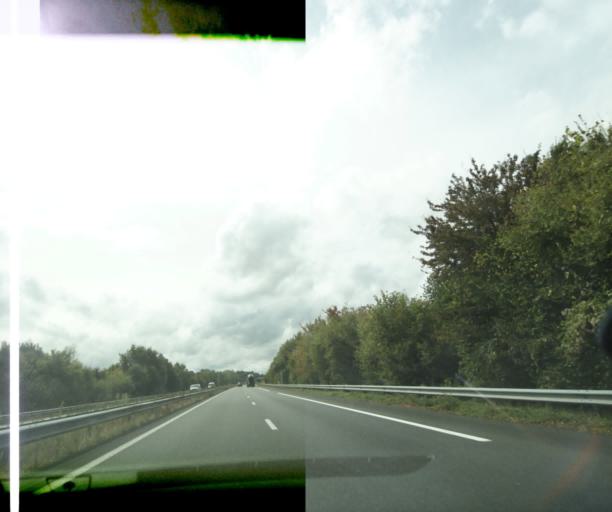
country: FR
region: Poitou-Charentes
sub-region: Departement de la Charente-Maritime
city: Saint-Genis-de-Saintonge
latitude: 45.4977
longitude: -0.6136
